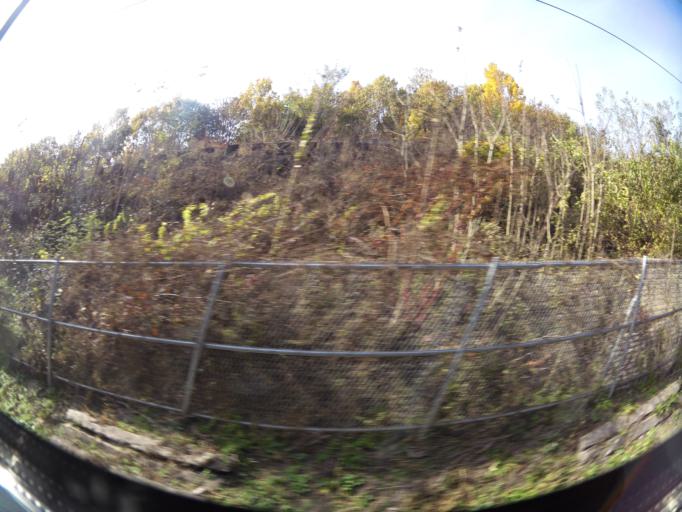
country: KR
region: Daejeon
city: Sintansin
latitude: 36.4775
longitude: 127.4223
